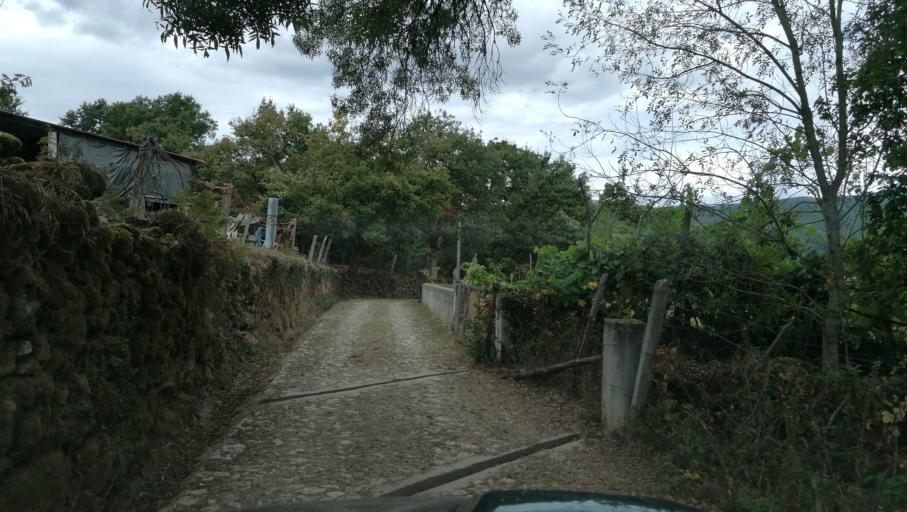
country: PT
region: Vila Real
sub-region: Ribeira de Pena
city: Sobreira
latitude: 41.5645
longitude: -7.7216
